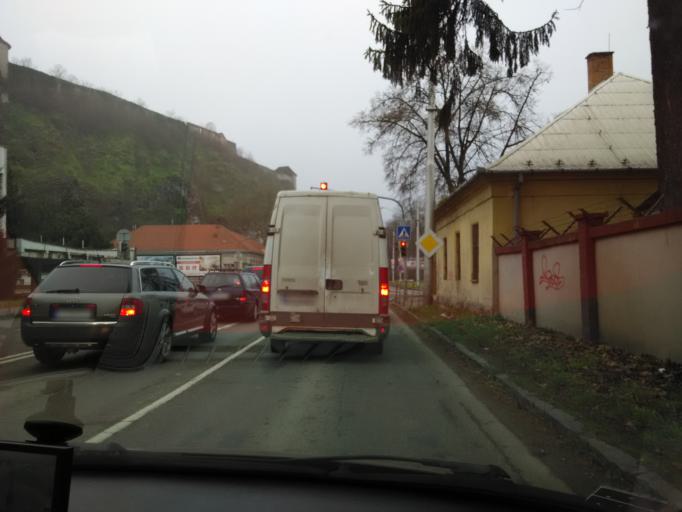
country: SK
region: Trenciansky
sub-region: Okres Trencin
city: Trencin
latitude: 48.8944
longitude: 18.0490
